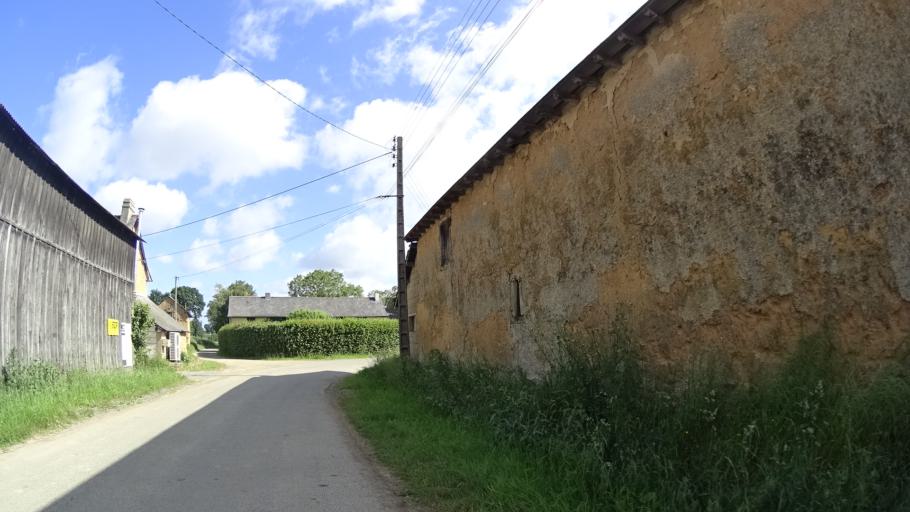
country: FR
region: Brittany
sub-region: Departement d'Ille-et-Vilaine
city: La Chapelle-des-Fougeretz
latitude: 48.2039
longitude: -1.7211
